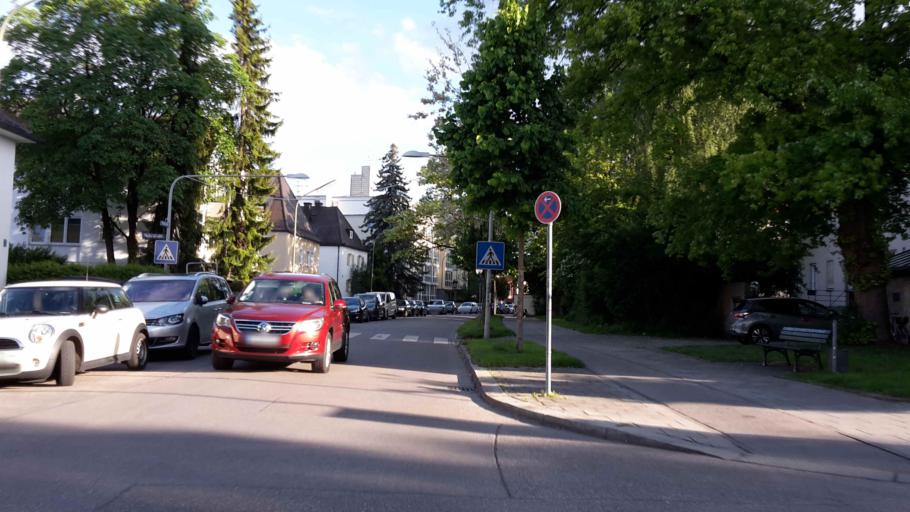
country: DE
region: Bavaria
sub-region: Upper Bavaria
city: Unterfoehring
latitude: 48.1952
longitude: 11.6189
